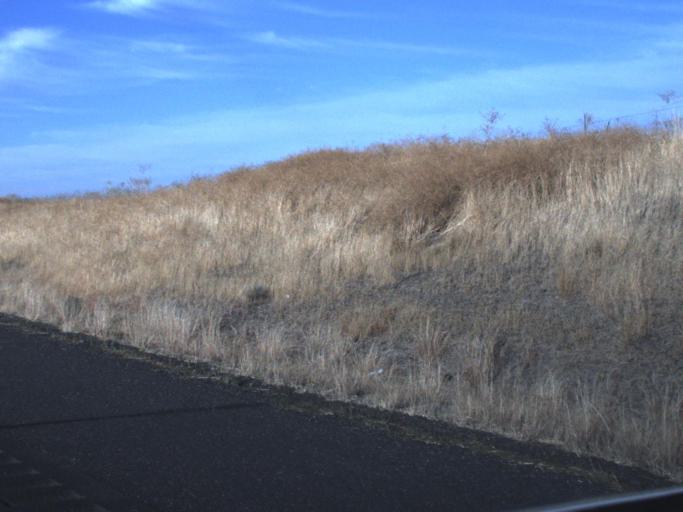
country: US
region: Washington
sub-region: Franklin County
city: Connell
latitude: 46.6390
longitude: -118.8650
